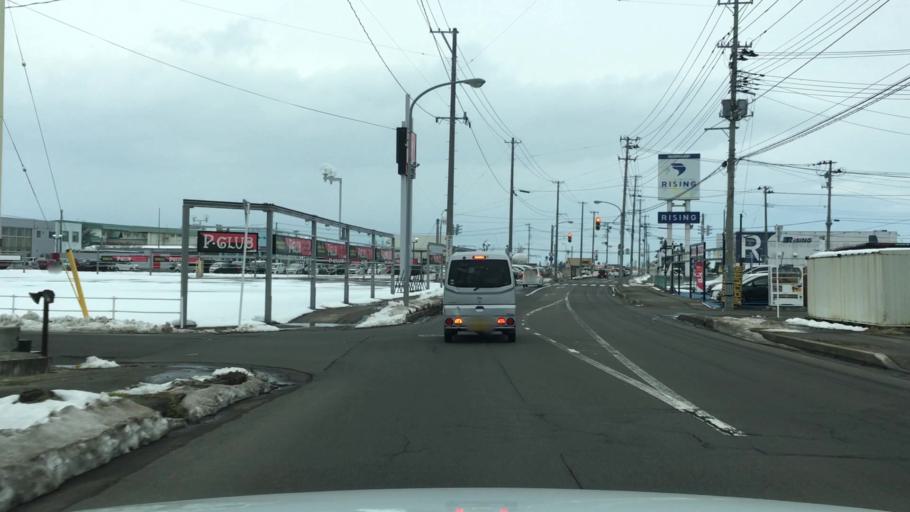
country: JP
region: Aomori
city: Hirosaki
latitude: 40.6100
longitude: 140.5045
